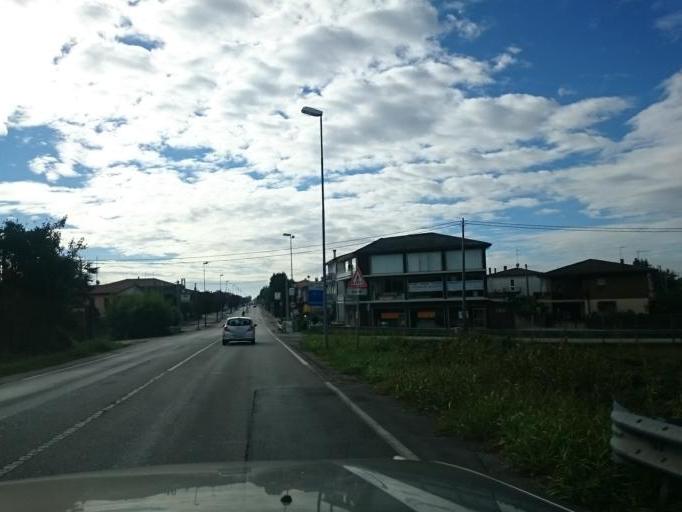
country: IT
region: Veneto
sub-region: Provincia di Padova
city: Albignasego
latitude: 45.3434
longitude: 11.9012
